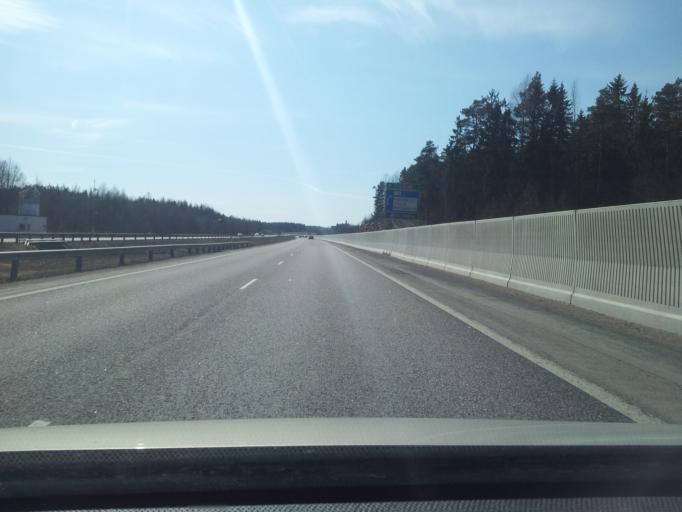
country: FI
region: Kymenlaakso
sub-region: Kotka-Hamina
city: Karhula
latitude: 60.5511
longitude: 26.9964
